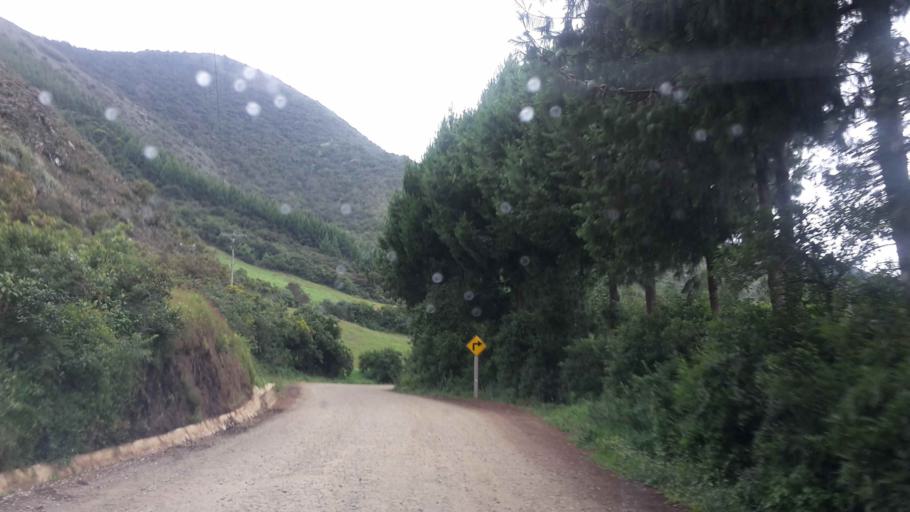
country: BO
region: Cochabamba
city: Totora
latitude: -17.5785
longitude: -65.2891
